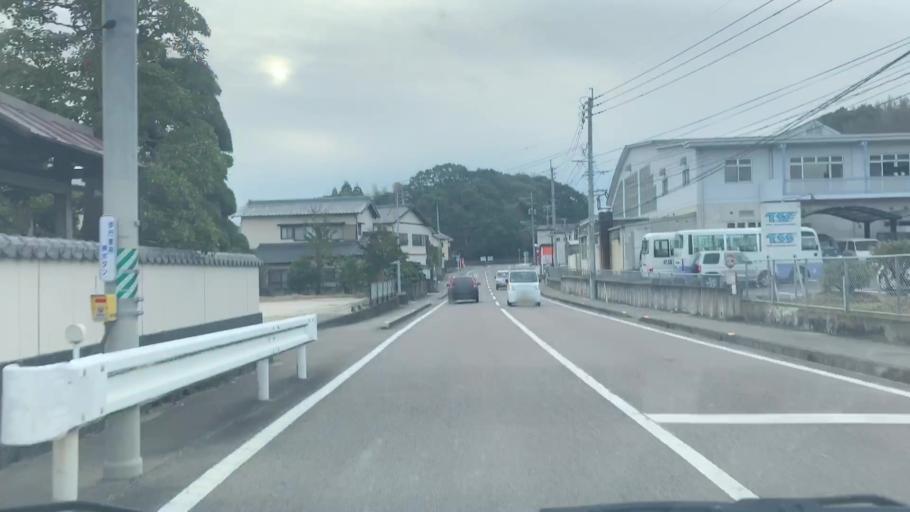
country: JP
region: Saga Prefecture
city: Takeocho-takeo
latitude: 33.1911
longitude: 130.0350
